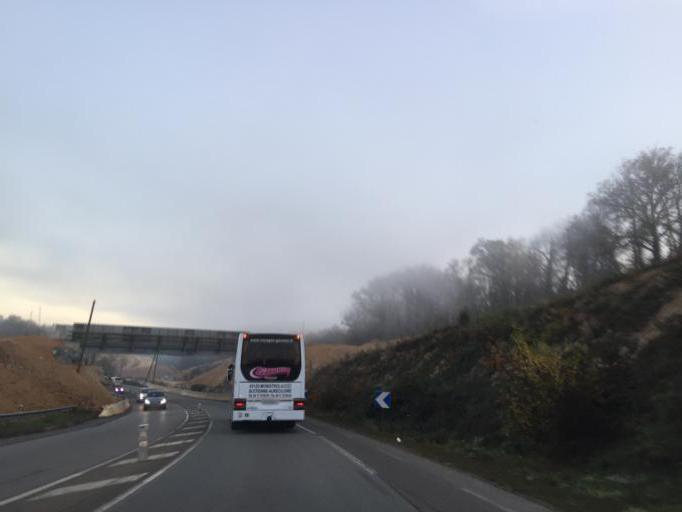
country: FR
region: Rhone-Alpes
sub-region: Departement de la Loire
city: Neulise
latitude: 45.8605
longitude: 4.1765
